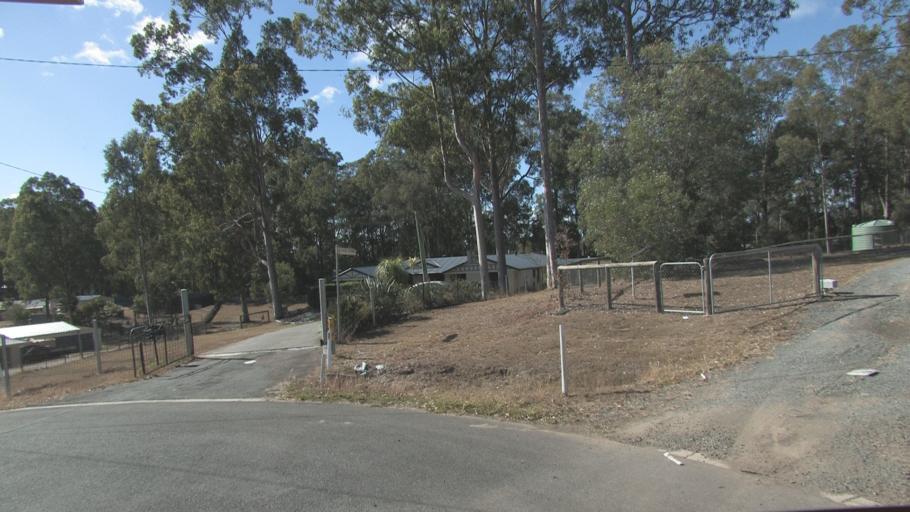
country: AU
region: Queensland
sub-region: Logan
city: Cedar Vale
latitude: -27.8781
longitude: 153.0077
